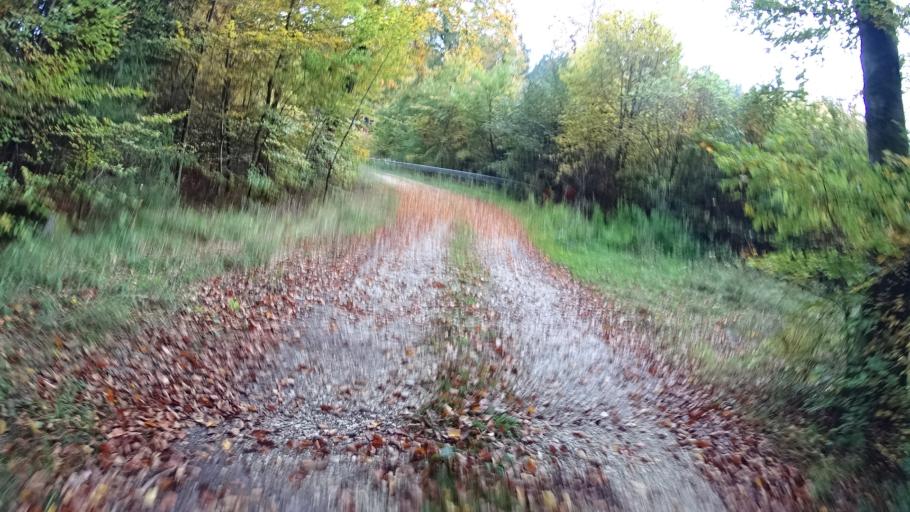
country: DE
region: Bavaria
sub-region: Upper Bavaria
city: Walting
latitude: 48.8739
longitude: 11.2600
